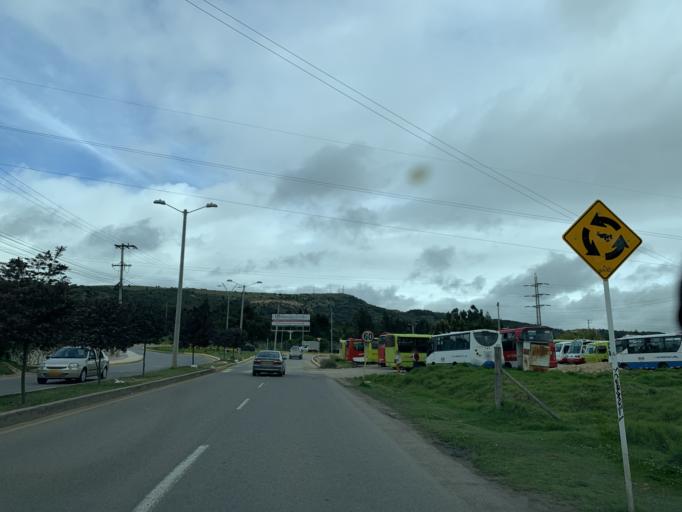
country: CO
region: Boyaca
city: Tunja
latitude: 5.5698
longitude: -73.3327
